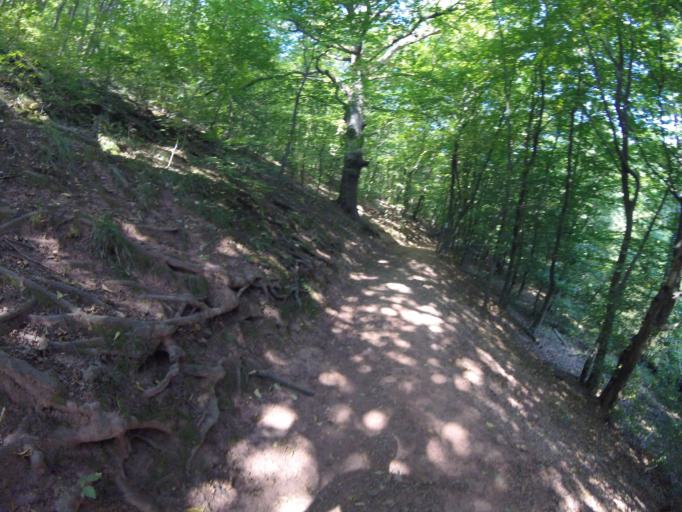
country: HU
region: Baranya
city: Pecs
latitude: 46.0884
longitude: 18.1803
